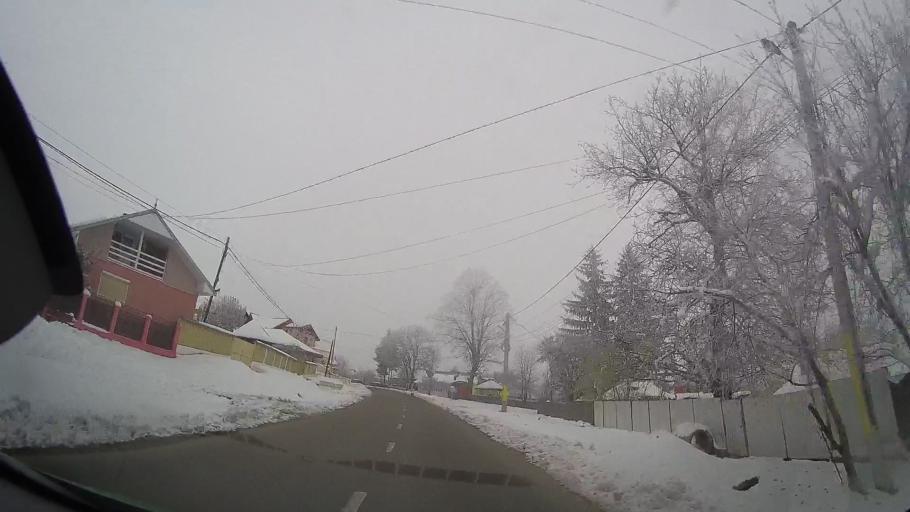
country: RO
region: Neamt
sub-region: Comuna Icusesti
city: Balusesti
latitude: 46.8637
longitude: 27.0038
